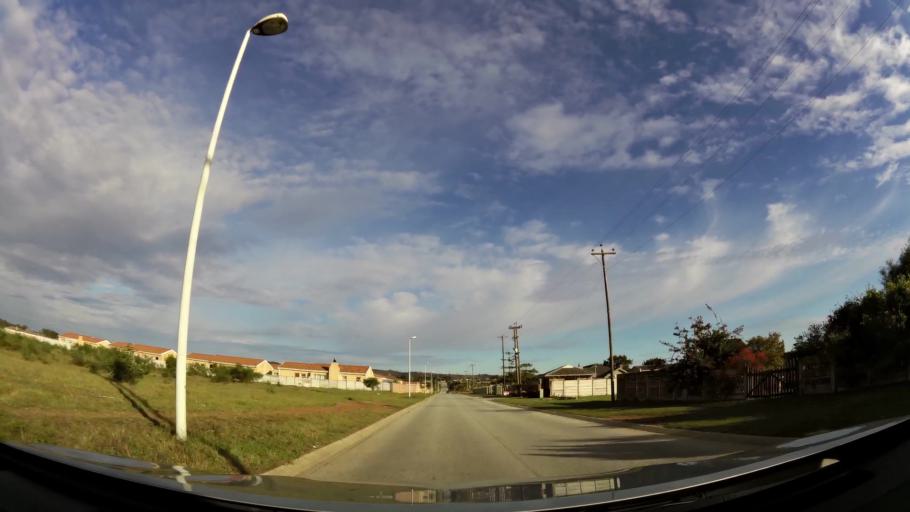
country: ZA
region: Eastern Cape
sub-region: Nelson Mandela Bay Metropolitan Municipality
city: Port Elizabeth
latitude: -33.9516
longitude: 25.4873
